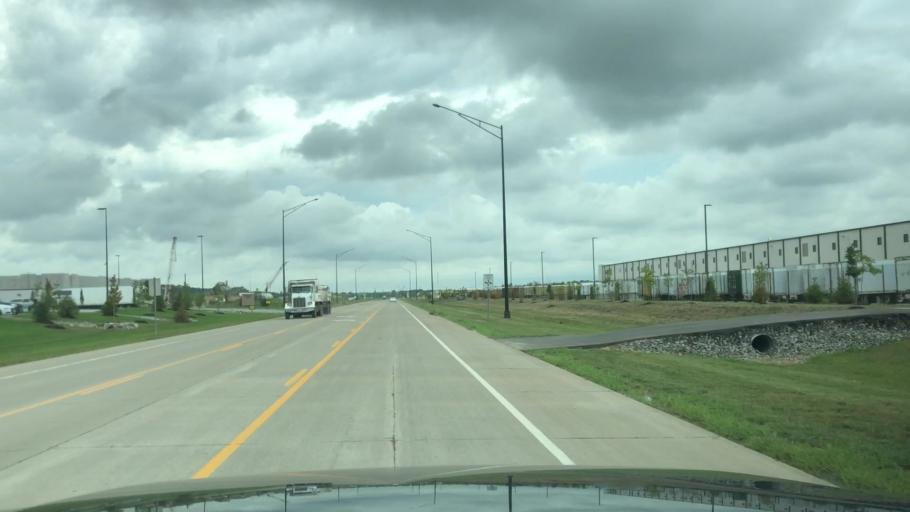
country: US
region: Missouri
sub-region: Saint Charles County
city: Saint Peters
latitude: 38.8124
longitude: -90.5650
